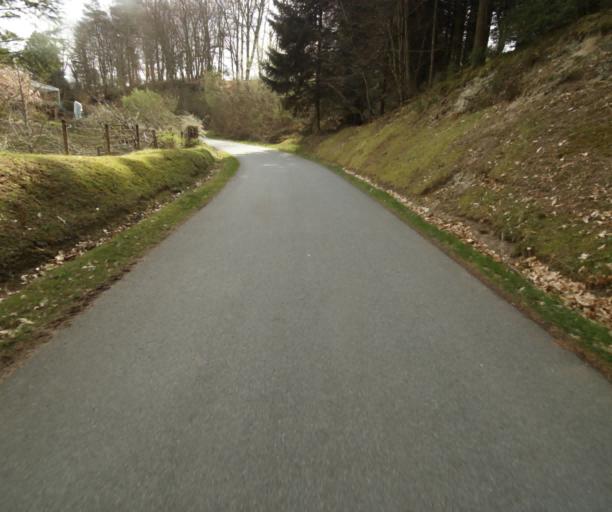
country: FR
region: Limousin
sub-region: Departement de la Correze
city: Correze
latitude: 45.3693
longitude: 1.8802
